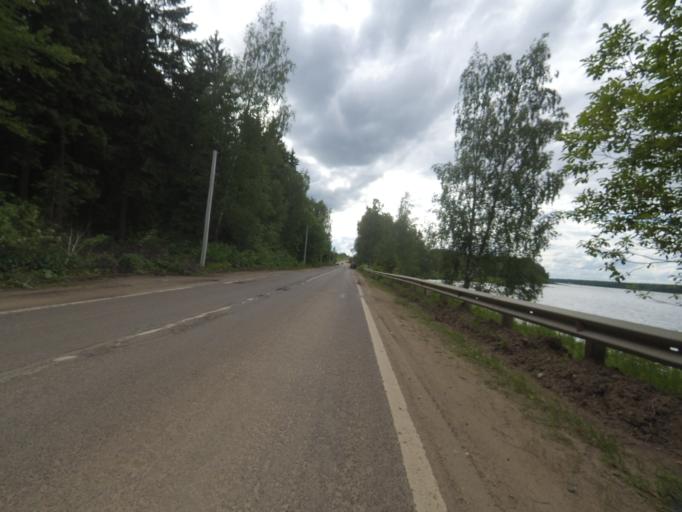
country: RU
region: Moskovskaya
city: Marfino
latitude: 56.1218
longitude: 37.5685
